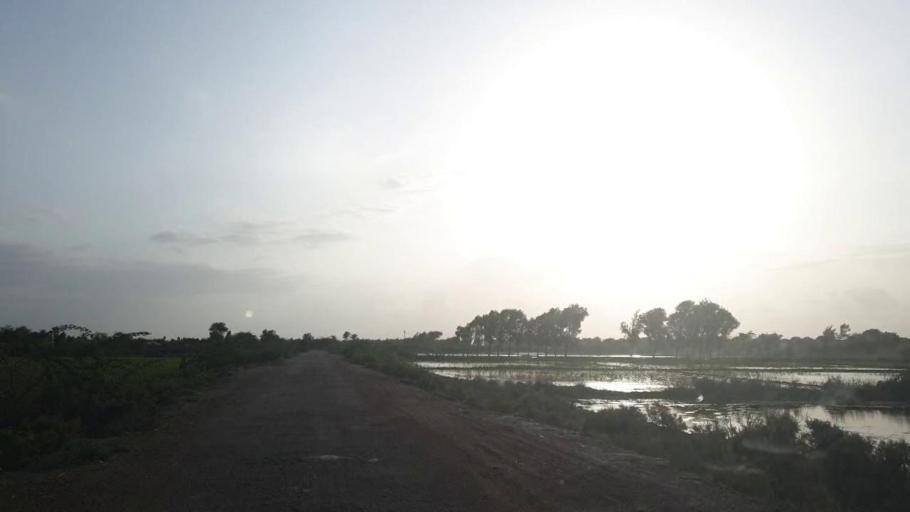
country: PK
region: Sindh
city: Kadhan
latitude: 24.6322
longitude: 69.1201
